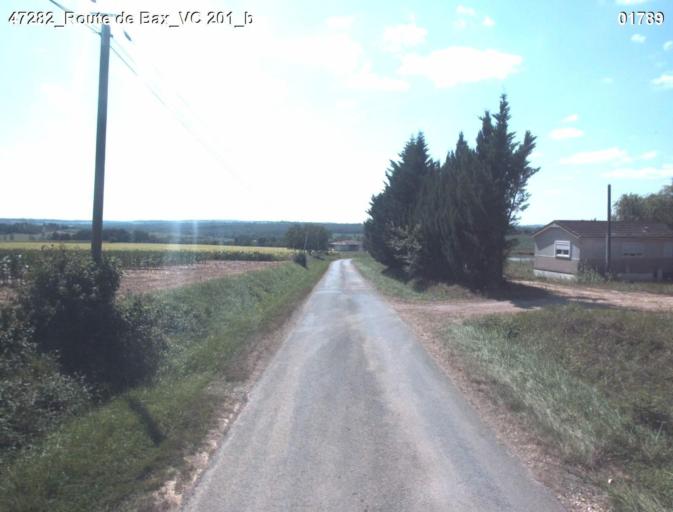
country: FR
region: Aquitaine
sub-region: Departement du Lot-et-Garonne
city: Laplume
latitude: 44.0834
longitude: 0.4988
